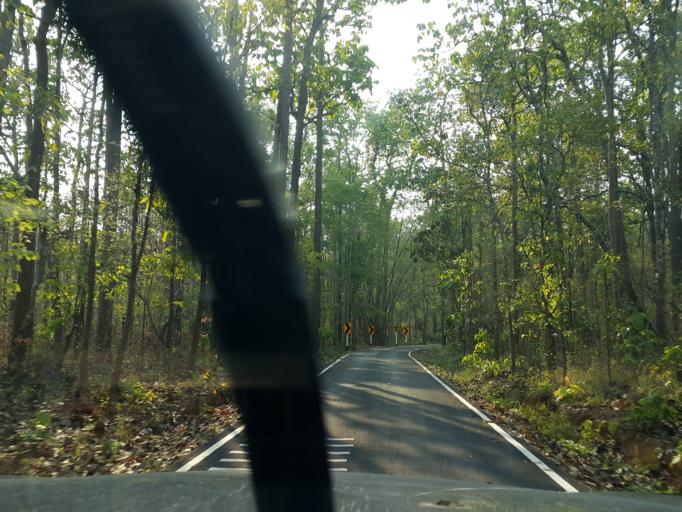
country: TH
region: Lamphun
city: Li
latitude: 17.6457
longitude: 98.8771
